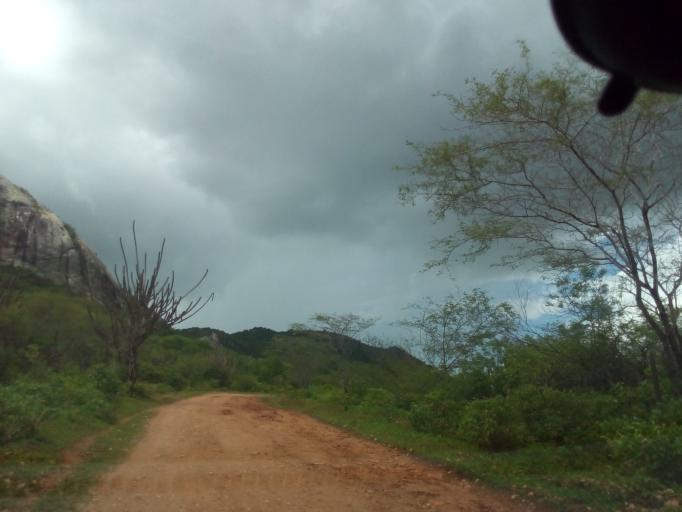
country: BR
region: Rio Grande do Norte
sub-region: Sao Paulo Do Potengi
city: Sao Paulo do Potengi
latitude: -5.9510
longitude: -35.9143
